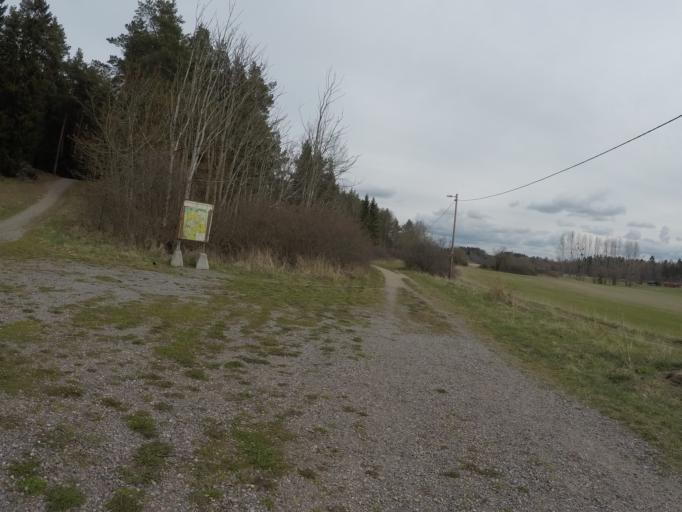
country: SE
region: Soedermanland
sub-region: Eskilstuna Kommun
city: Torshalla
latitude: 59.4253
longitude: 16.4902
